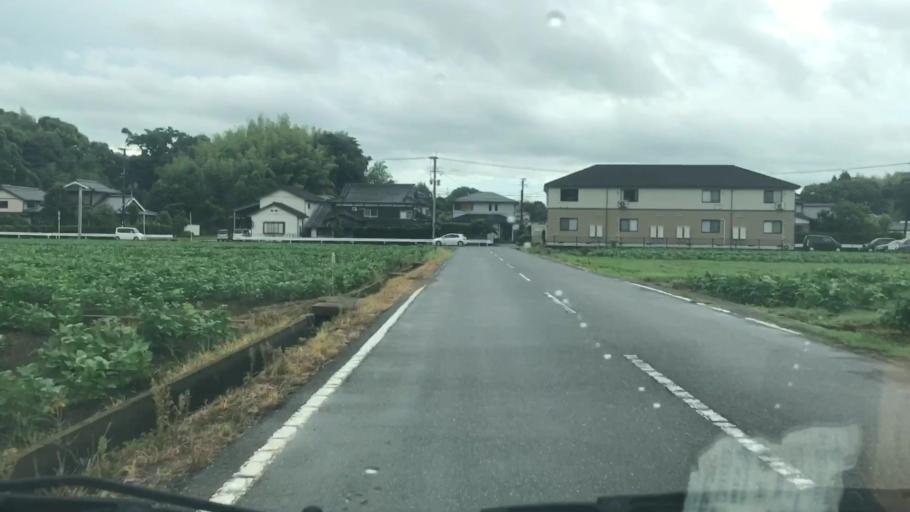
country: JP
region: Saga Prefecture
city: Takeocho-takeo
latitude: 33.1928
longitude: 130.0355
